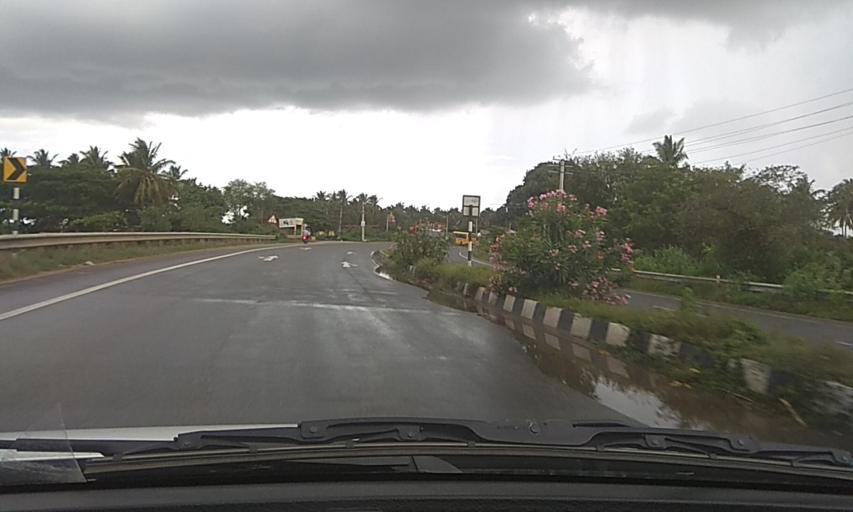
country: IN
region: Karnataka
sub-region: Mysore
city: Mysore
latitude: 12.2380
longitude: 76.6615
